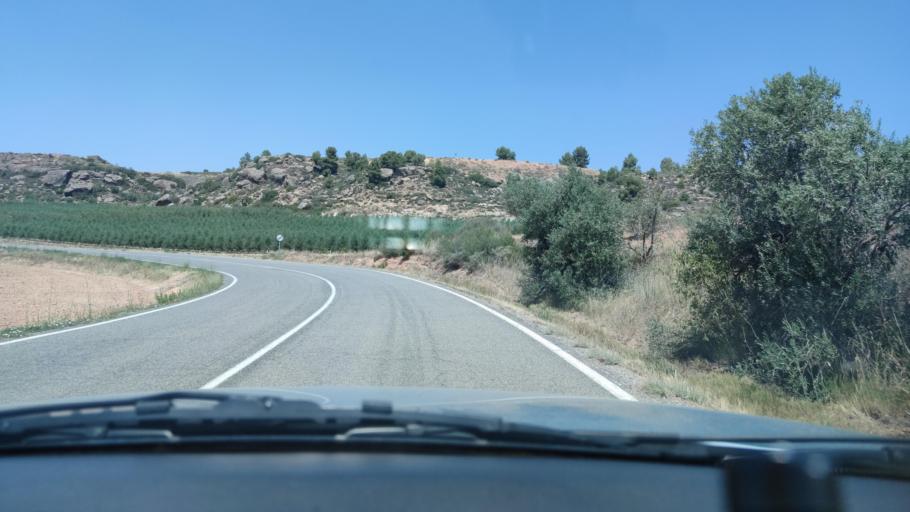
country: ES
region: Catalonia
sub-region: Provincia de Lleida
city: el Cogul
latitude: 41.4308
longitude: 0.6587
